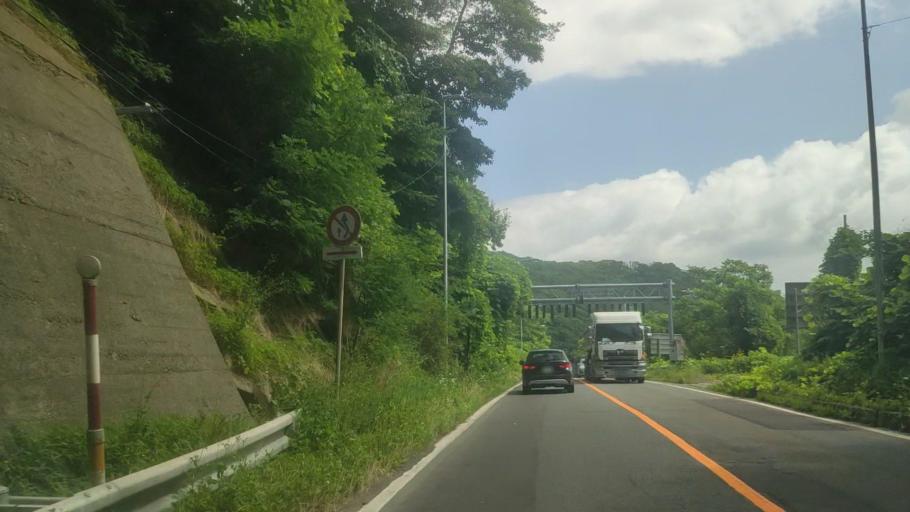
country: JP
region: Hokkaido
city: Date
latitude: 42.5630
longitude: 140.7420
